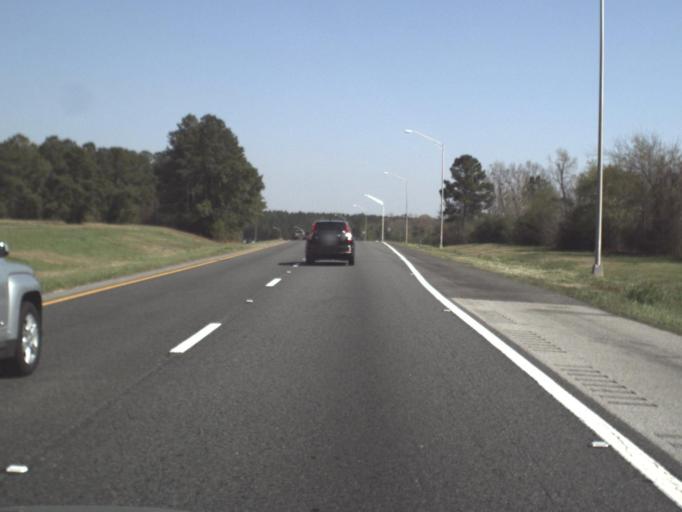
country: US
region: Florida
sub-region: Jackson County
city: Sneads
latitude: 30.6395
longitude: -84.9971
